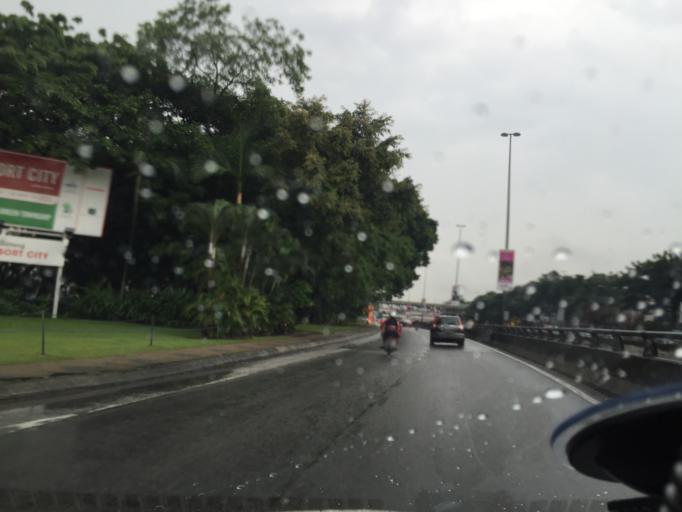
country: MY
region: Selangor
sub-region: Petaling
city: Petaling Jaya
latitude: 3.0744
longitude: 101.6131
